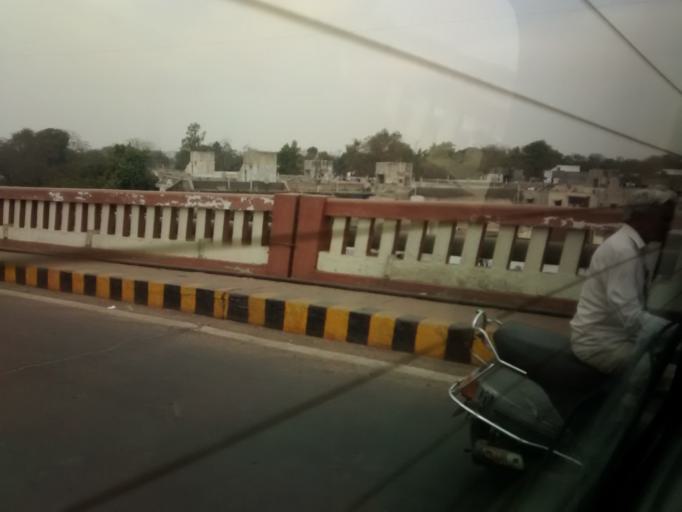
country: IN
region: Gujarat
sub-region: Ahmadabad
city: Ahmedabad
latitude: 23.0695
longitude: 72.5862
